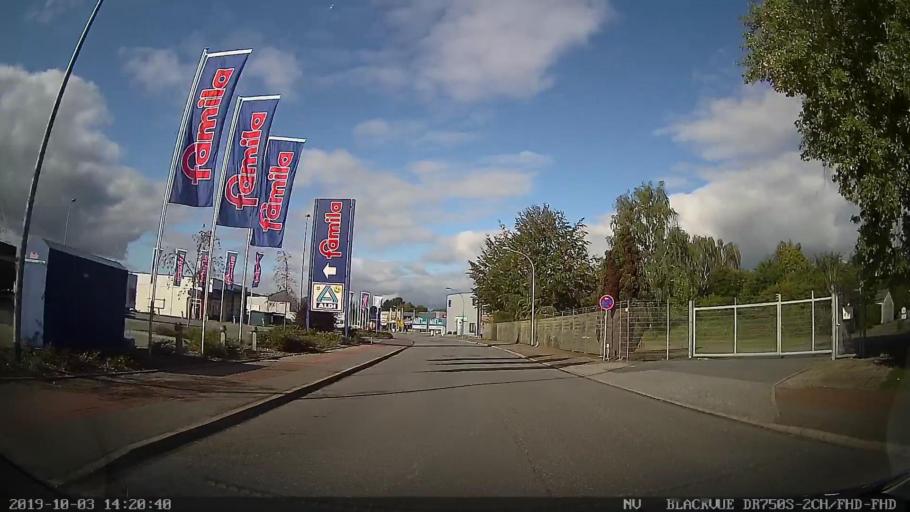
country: DE
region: Schleswig-Holstein
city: Pinneberg
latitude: 53.6723
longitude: 9.8023
